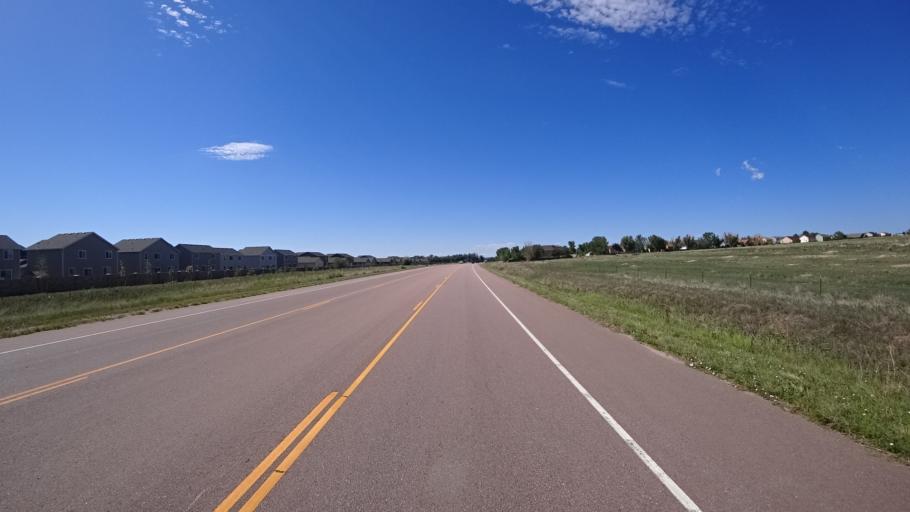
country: US
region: Colorado
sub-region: El Paso County
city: Security-Widefield
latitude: 38.7430
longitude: -104.6483
